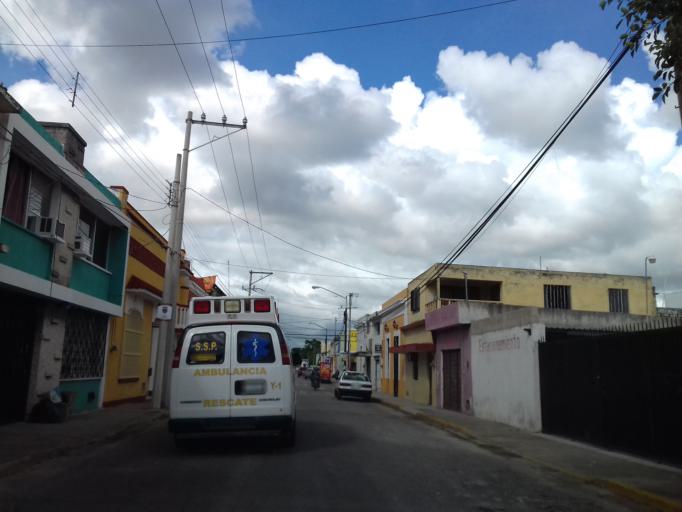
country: MX
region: Yucatan
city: Merida
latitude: 20.9717
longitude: -89.6298
